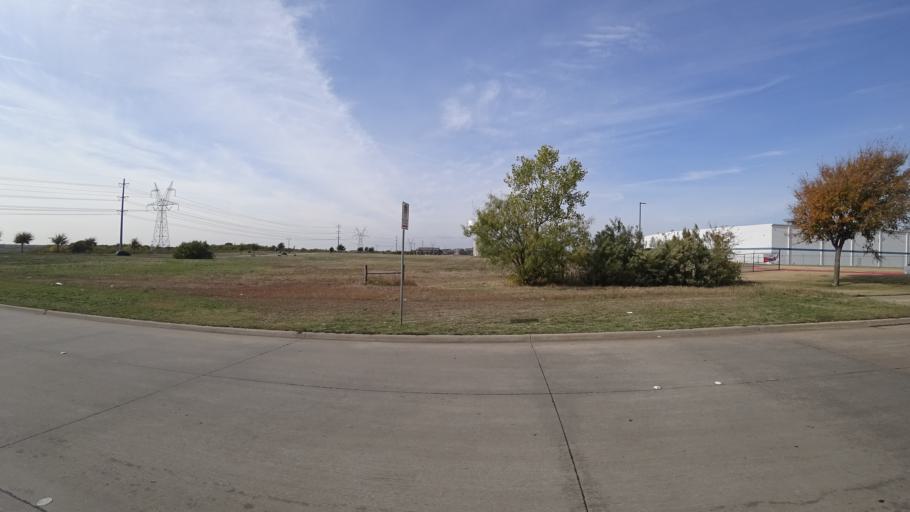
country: US
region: Texas
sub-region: Denton County
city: The Colony
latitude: 33.0619
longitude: -96.8714
